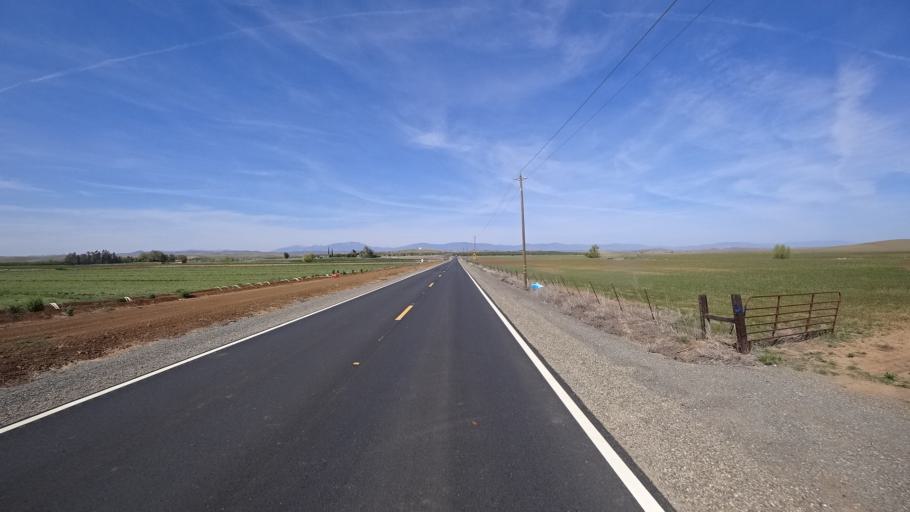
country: US
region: California
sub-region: Glenn County
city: Willows
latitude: 39.5241
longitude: -122.2962
